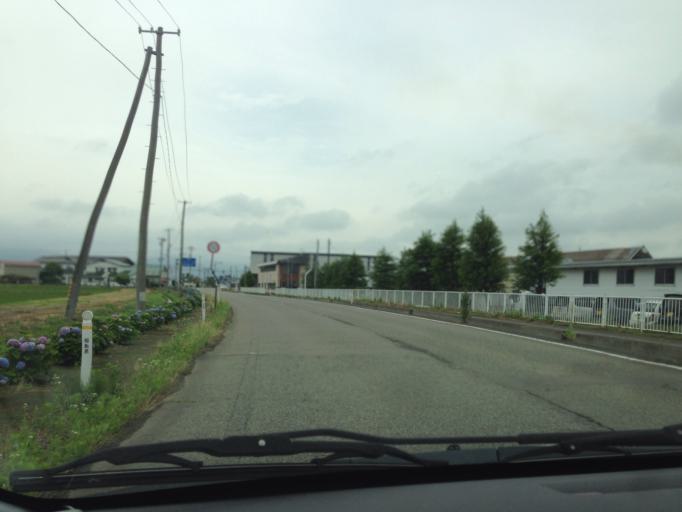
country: JP
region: Fukushima
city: Kitakata
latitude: 37.5561
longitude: 139.8911
